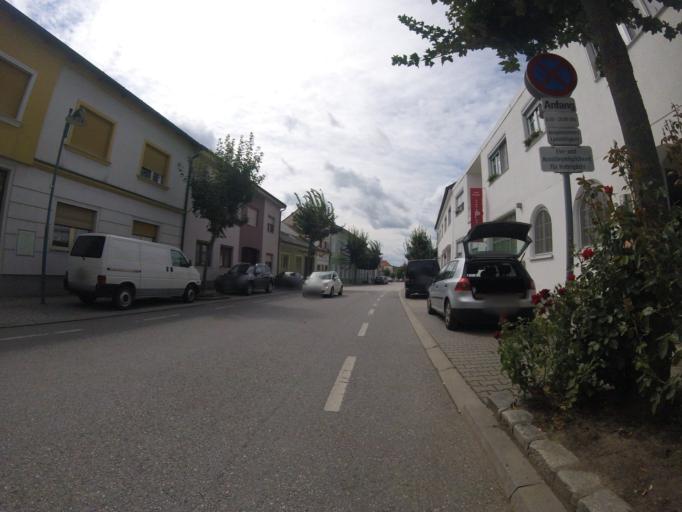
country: AT
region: Burgenland
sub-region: Politischer Bezirk Neusiedl am See
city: Jois
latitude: 47.9604
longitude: 16.7959
